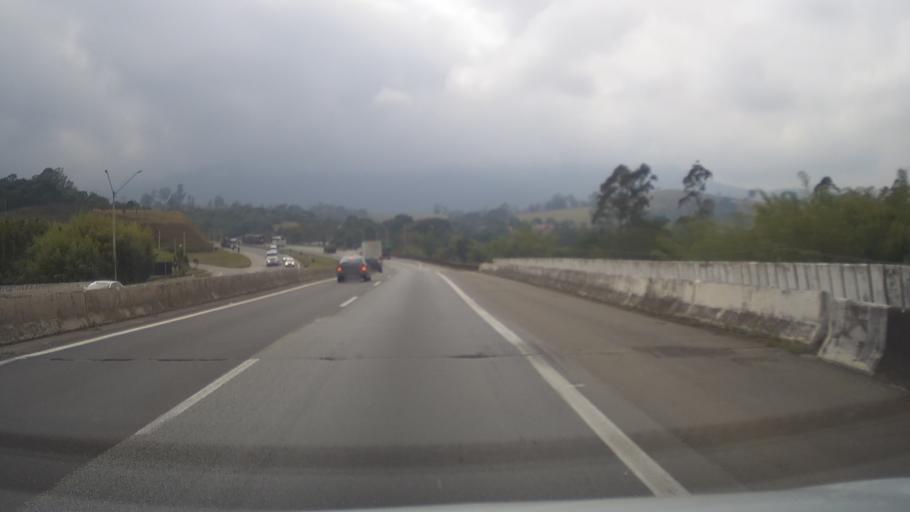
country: BR
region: Minas Gerais
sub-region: Extrema
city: Extrema
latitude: -22.8814
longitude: -46.3917
